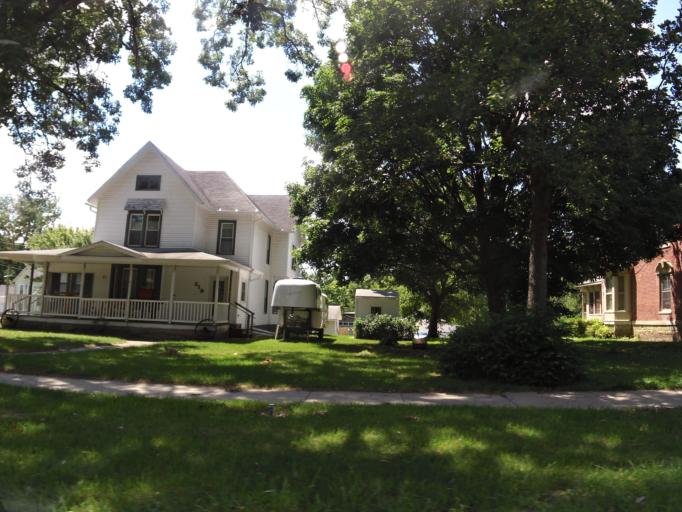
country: US
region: Iowa
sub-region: Buchanan County
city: Independence
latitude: 42.4658
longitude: -91.8918
